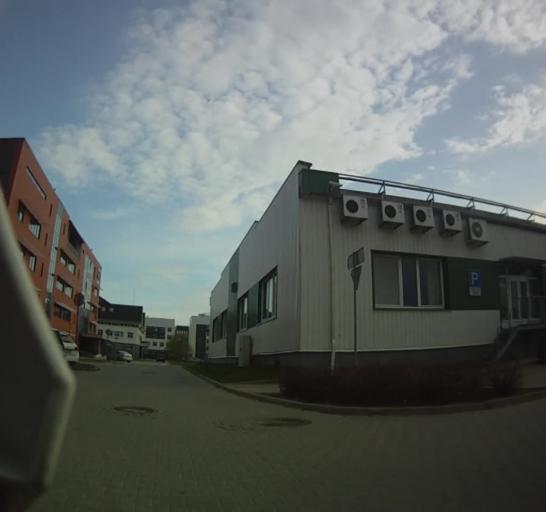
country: LV
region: Riga
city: Riga
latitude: 56.9780
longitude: 24.1310
